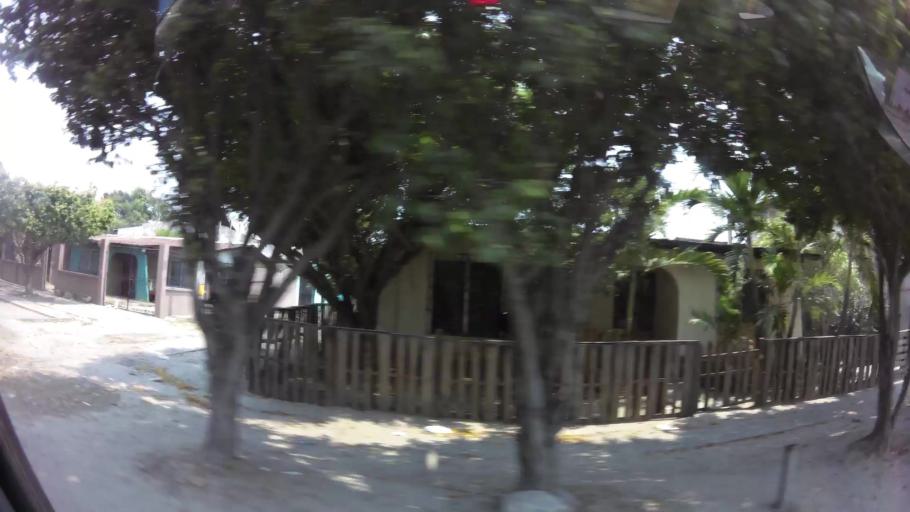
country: HN
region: Cortes
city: San Pedro Sula
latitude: 15.4892
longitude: -87.9883
